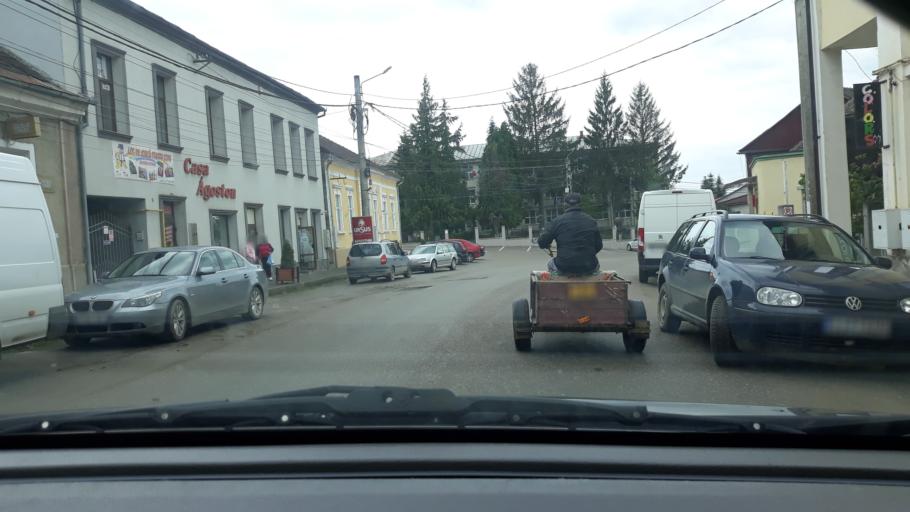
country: RO
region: Salaj
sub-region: Comuna Cehu Silvaniei
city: Cehu Silvaniei
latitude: 47.4114
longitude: 23.1767
